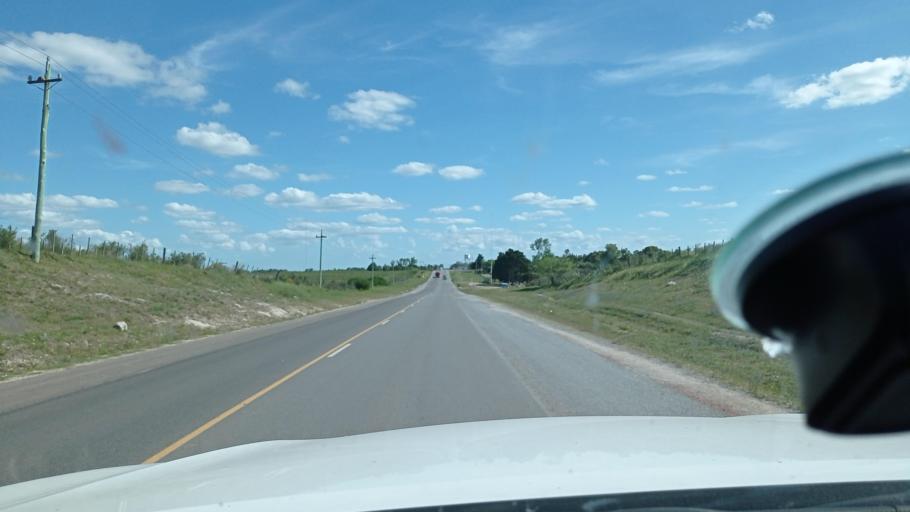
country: UY
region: Florida
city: Florida
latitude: -34.0794
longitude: -56.2352
